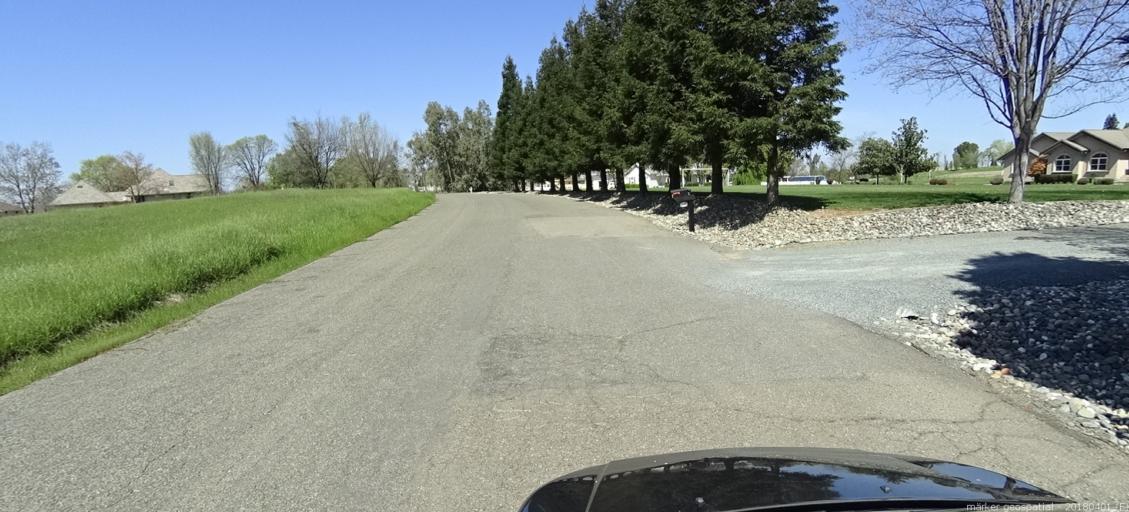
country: US
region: California
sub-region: Sacramento County
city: Wilton
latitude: 38.4156
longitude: -121.2169
